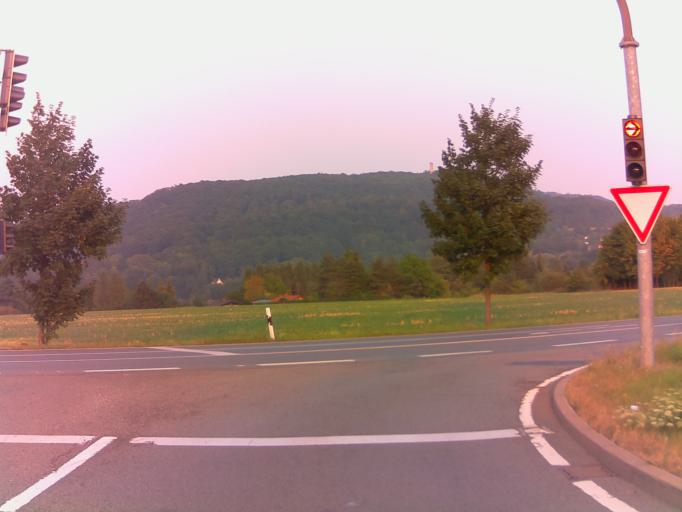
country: DE
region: Thuringia
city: Bad Berka
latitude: 50.9056
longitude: 11.2765
